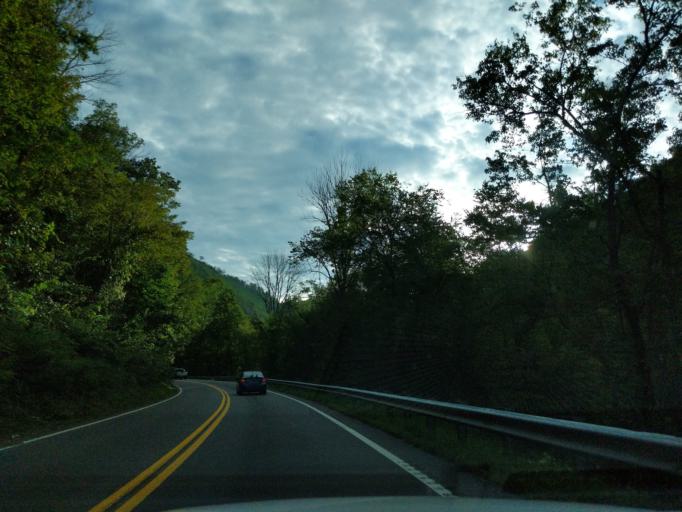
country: US
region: Tennessee
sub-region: Polk County
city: Benton
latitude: 35.0816
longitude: -84.5249
